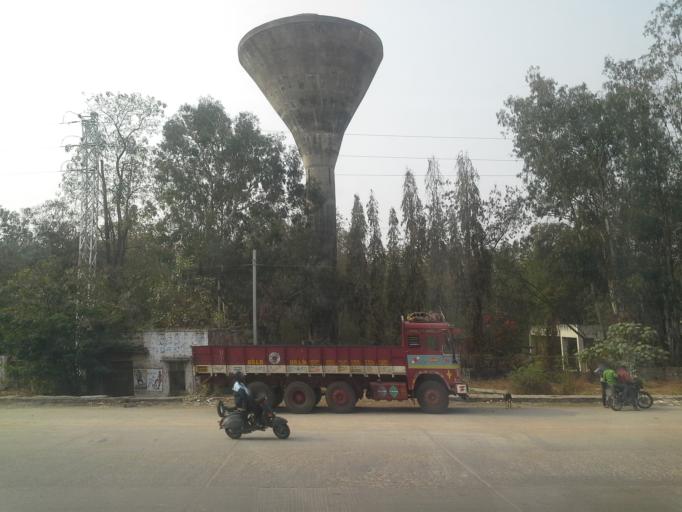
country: IN
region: Telangana
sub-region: Medak
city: Patancheru
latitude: 17.5244
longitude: 78.2723
